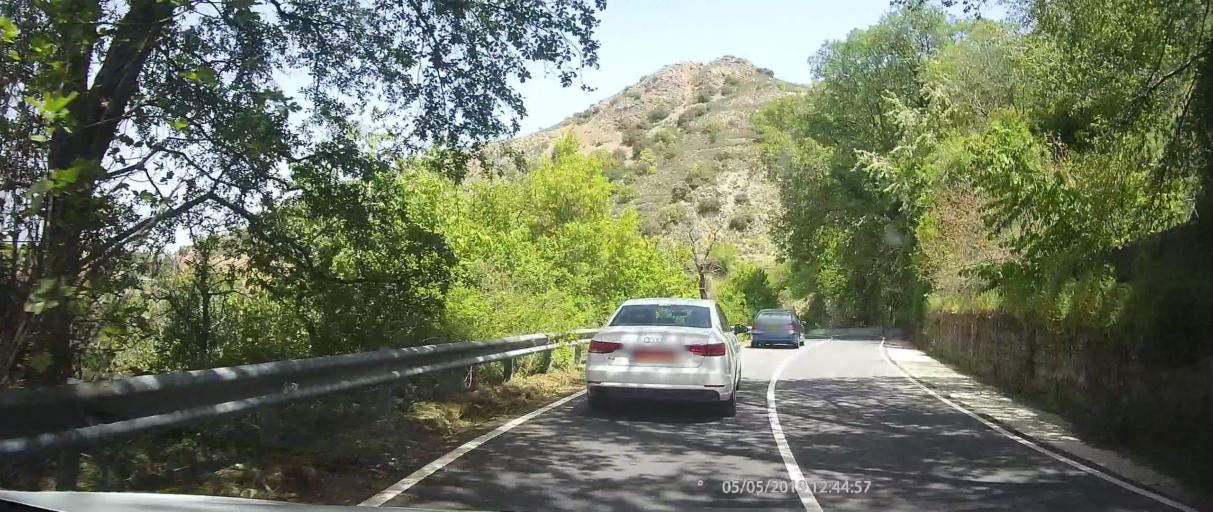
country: CY
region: Lefkosia
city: Kakopetria
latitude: 34.9660
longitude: 32.8208
